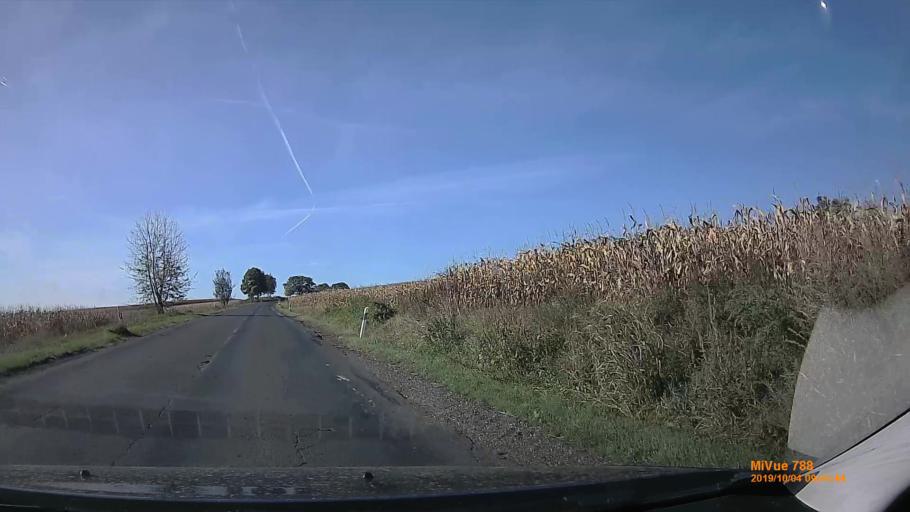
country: HU
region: Somogy
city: Kaposvar
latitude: 46.4381
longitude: 17.7927
